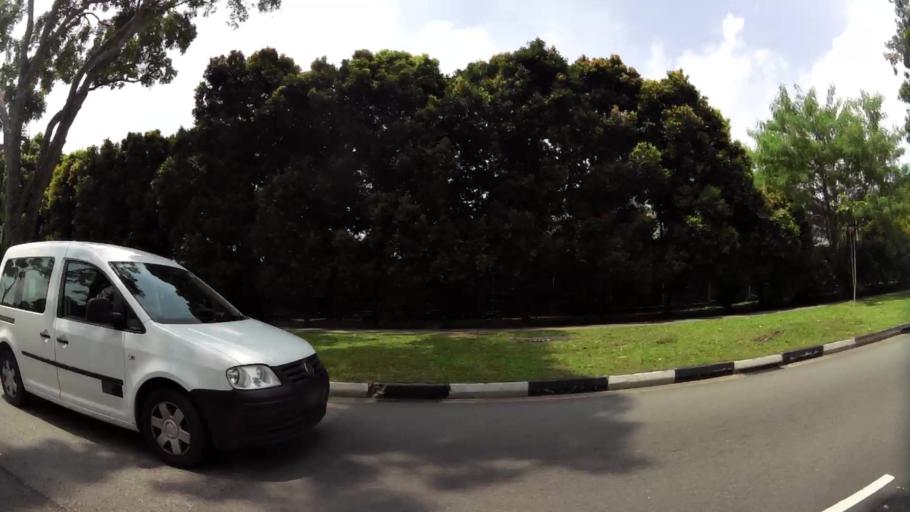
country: MY
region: Johor
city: Kampung Pasir Gudang Baru
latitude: 1.3801
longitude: 103.9784
